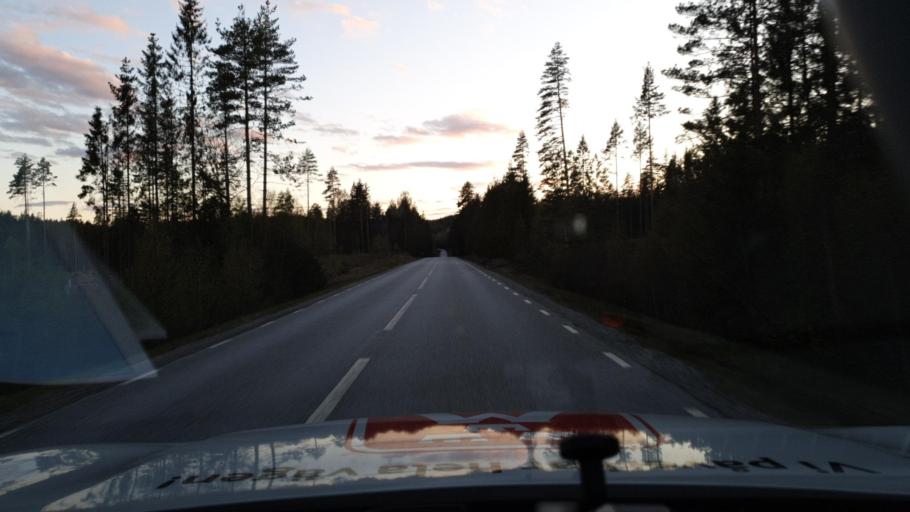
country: SE
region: Dalarna
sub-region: Smedjebackens Kommun
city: Smedjebacken
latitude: 59.9203
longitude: 15.4265
